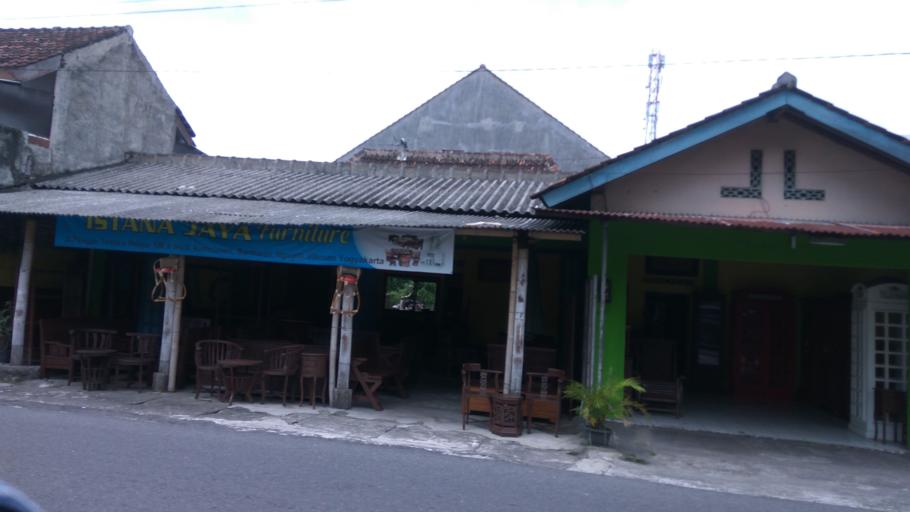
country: ID
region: Daerah Istimewa Yogyakarta
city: Melati
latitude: -7.7213
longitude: 110.3827
